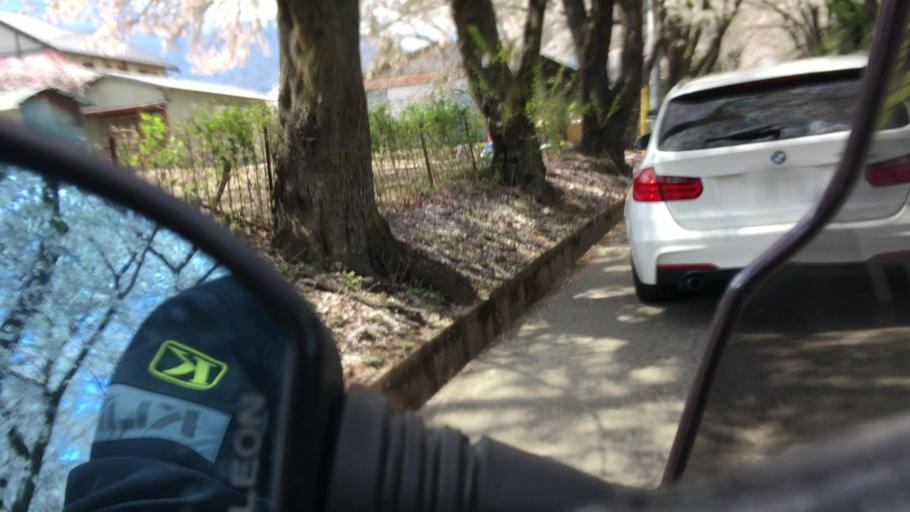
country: JP
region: Yamanashi
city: Nirasaki
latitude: 35.7767
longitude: 138.3441
